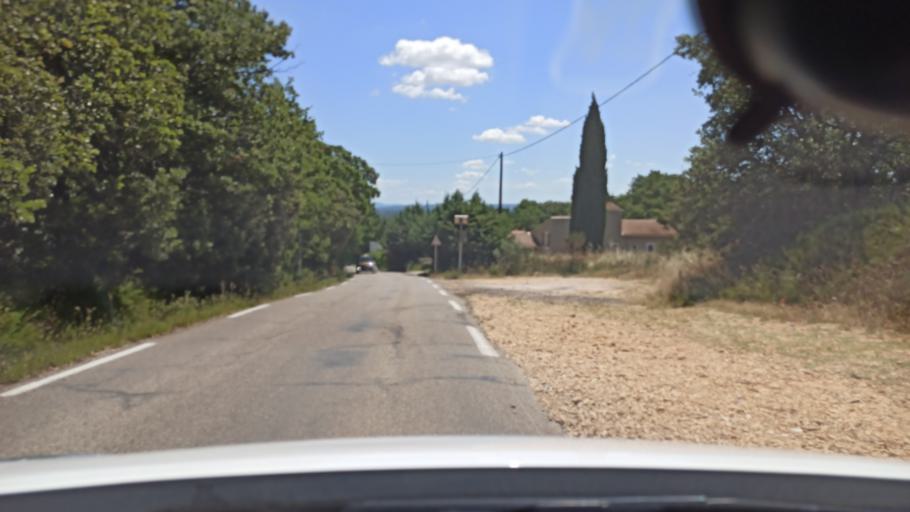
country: FR
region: Provence-Alpes-Cote d'Azur
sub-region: Departement du Vaucluse
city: Caumont-sur-Durance
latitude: 43.9006
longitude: 4.9333
